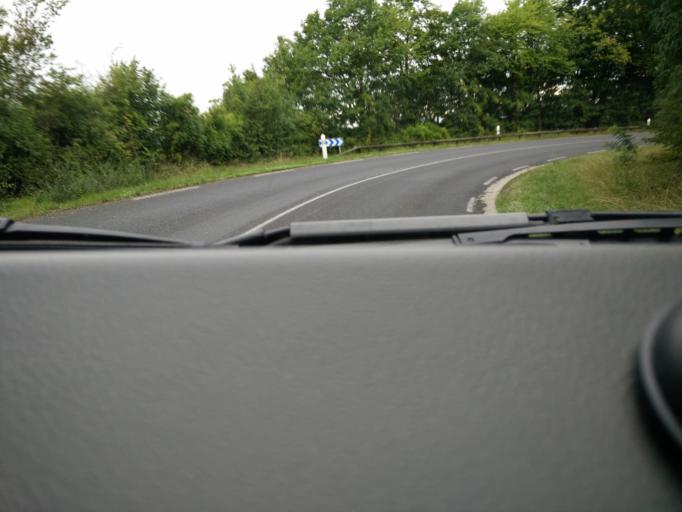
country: FR
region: Lorraine
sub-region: Departement de Meurthe-et-Moselle
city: Montauville
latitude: 48.9379
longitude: 5.8842
